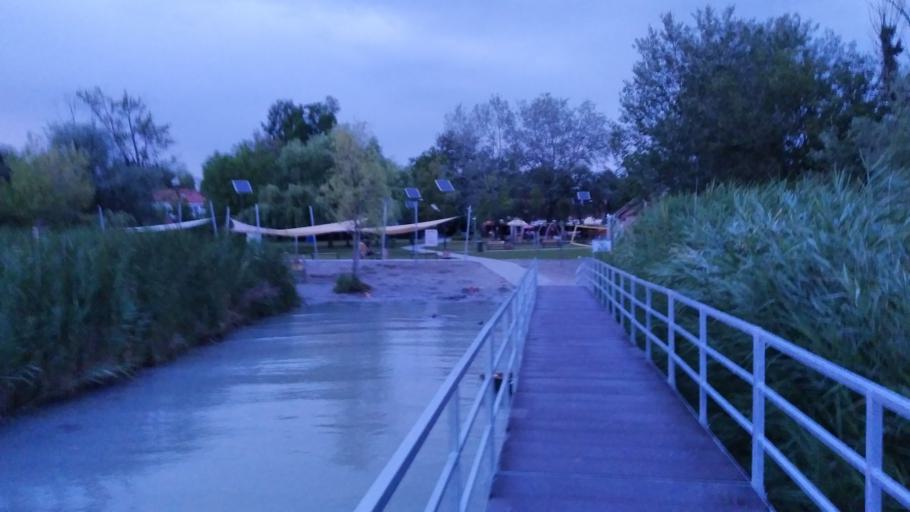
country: HU
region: Veszprem
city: Balatonkenese
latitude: 47.0255
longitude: 18.1262
